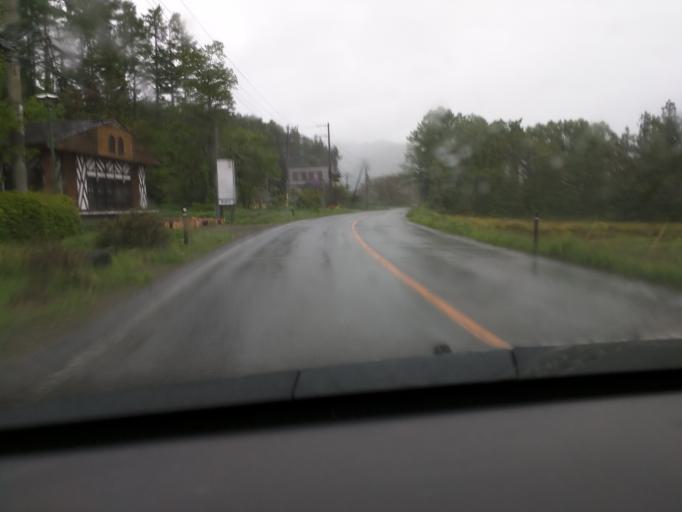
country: JP
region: Fukushima
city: Inawashiro
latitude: 37.5914
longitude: 140.1248
